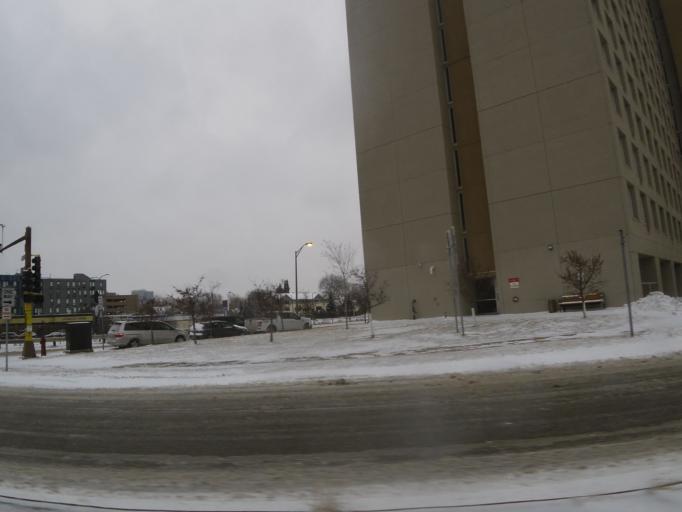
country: US
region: Minnesota
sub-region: Hennepin County
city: Minneapolis
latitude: 44.9637
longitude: -93.2361
